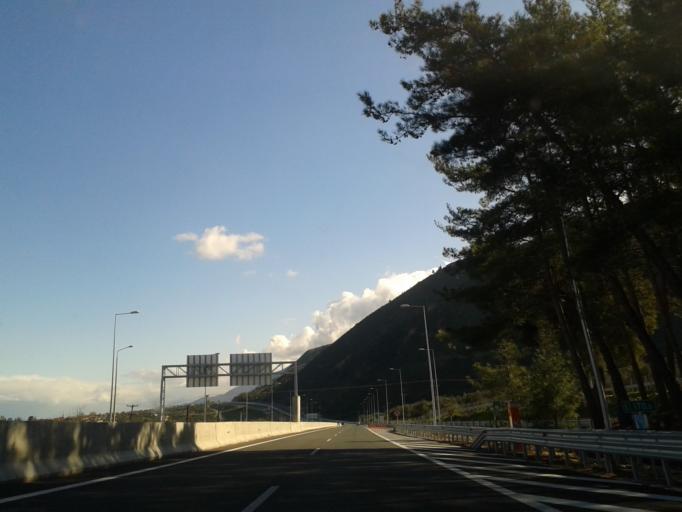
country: GR
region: West Greece
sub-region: Nomos Achaias
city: Temeni
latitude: 38.2200
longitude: 22.1048
